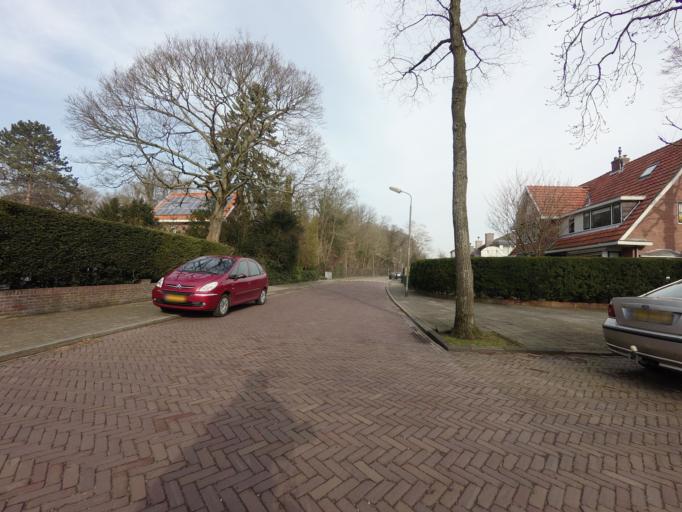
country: NL
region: North Holland
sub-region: Gemeente Heemstede
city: Heemstede
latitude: 52.3530
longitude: 4.6161
